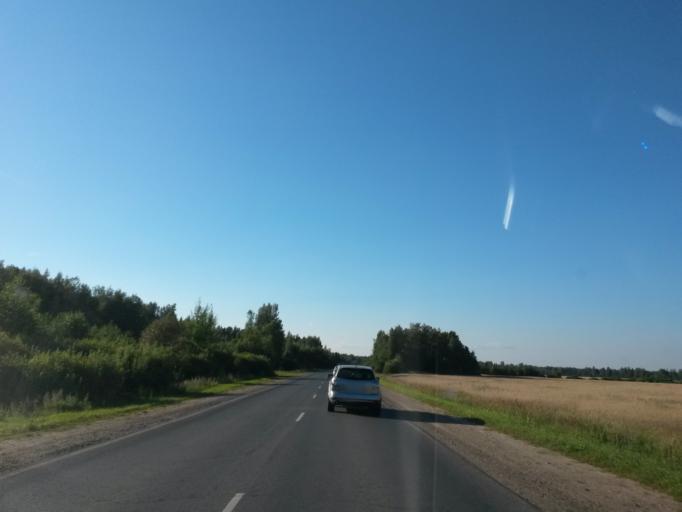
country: RU
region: Ivanovo
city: Novo-Talitsy
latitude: 57.0329
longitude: 40.7499
